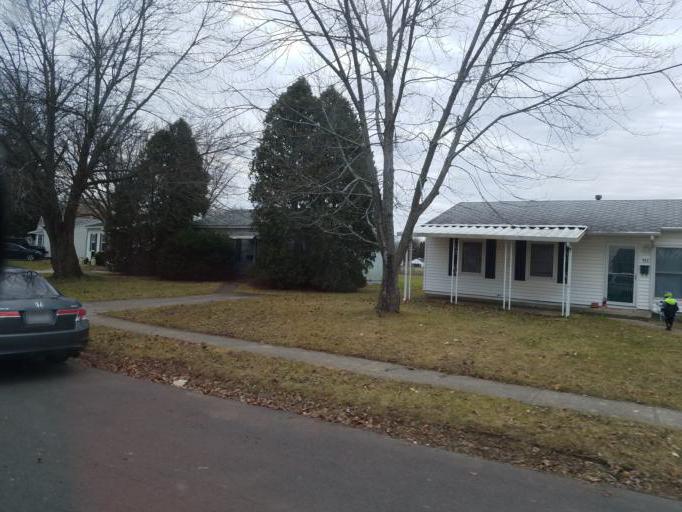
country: US
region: Ohio
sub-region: Marion County
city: Marion
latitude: 40.6067
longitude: -83.1145
